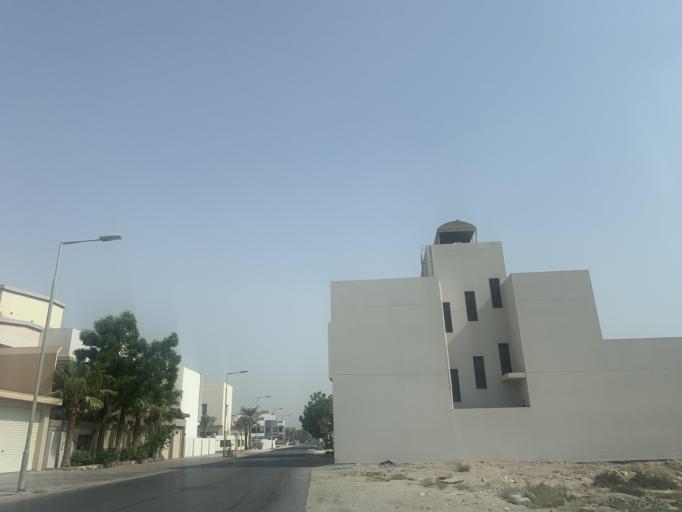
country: BH
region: Manama
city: Jidd Hafs
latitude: 26.2111
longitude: 50.4693
